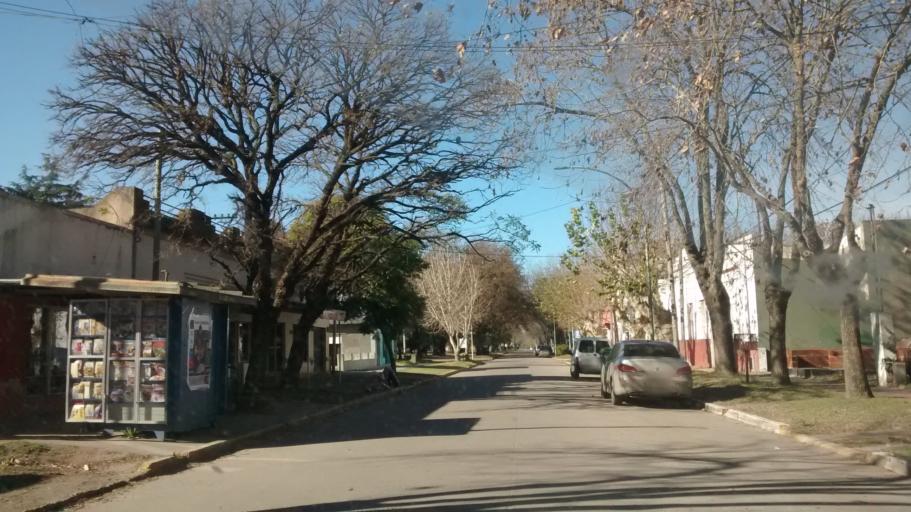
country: AR
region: Buenos Aires
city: Pila
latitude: -36.0034
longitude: -58.1430
